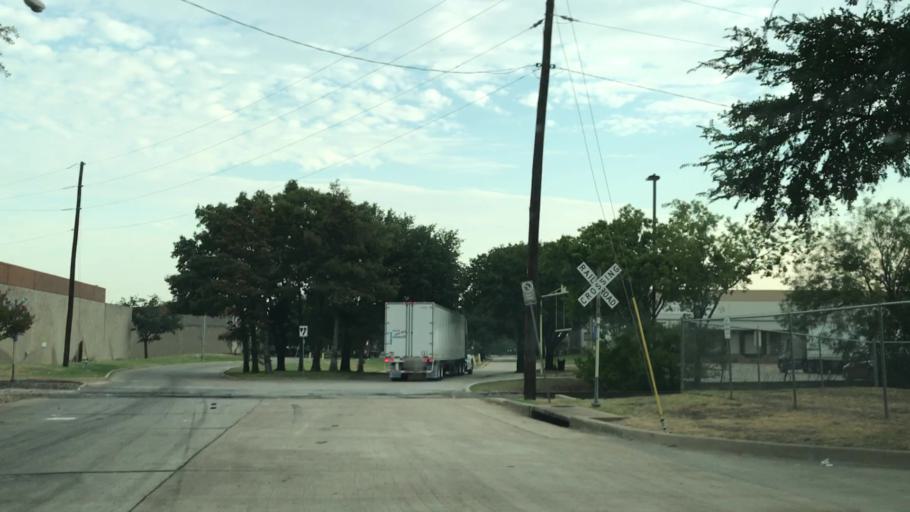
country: US
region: Texas
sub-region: Dallas County
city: Cockrell Hill
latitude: 32.7724
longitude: -96.8790
